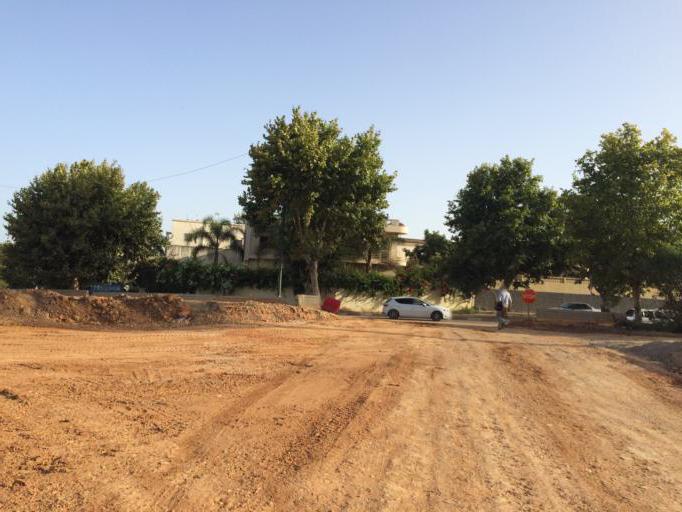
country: MA
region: Rabat-Sale-Zemmour-Zaer
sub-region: Rabat
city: Rabat
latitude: 33.9999
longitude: -6.8248
